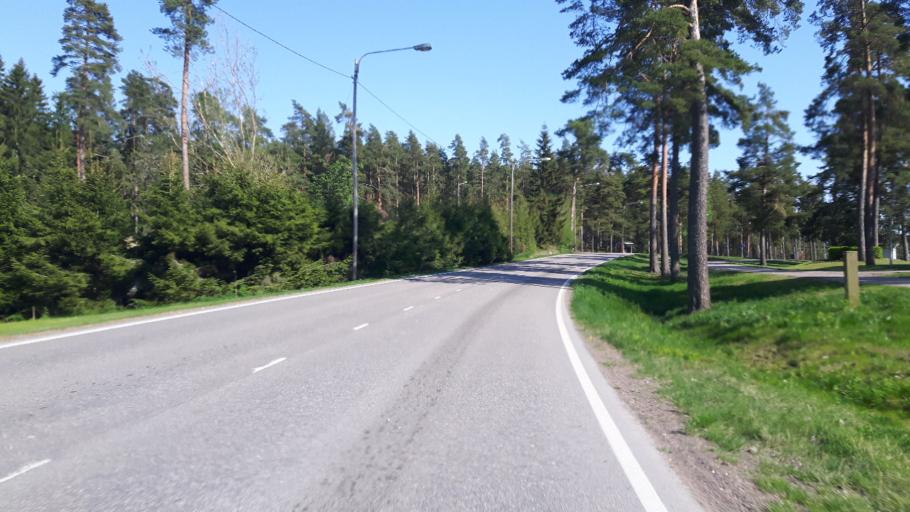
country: FI
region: Kymenlaakso
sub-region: Kotka-Hamina
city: Broby
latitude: 60.4902
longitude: 26.7445
